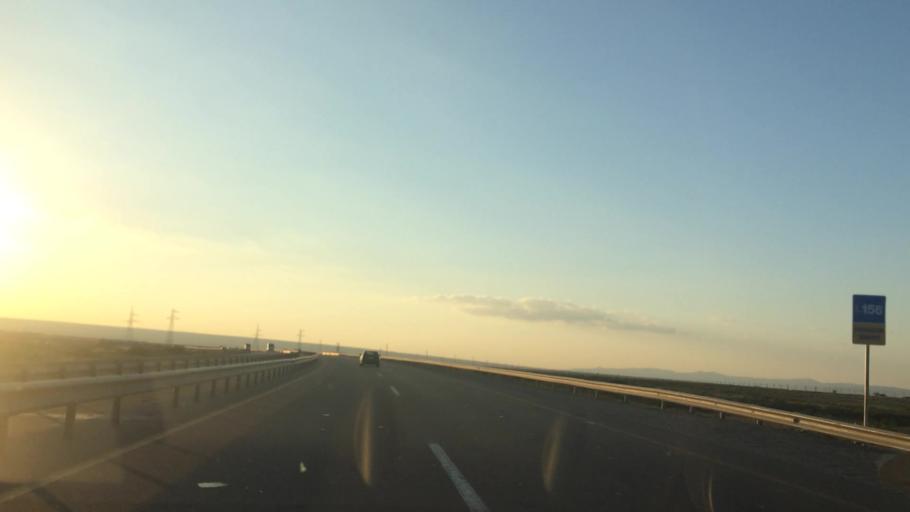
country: AZ
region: Baki
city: Qobustan
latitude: 39.9825
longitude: 49.2310
